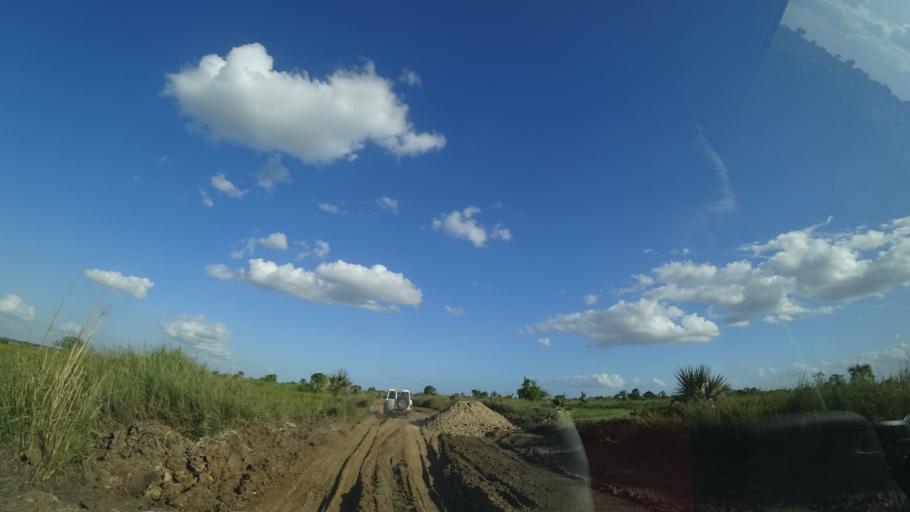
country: MZ
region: Sofala
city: Dondo
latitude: -19.4101
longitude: 34.5663
